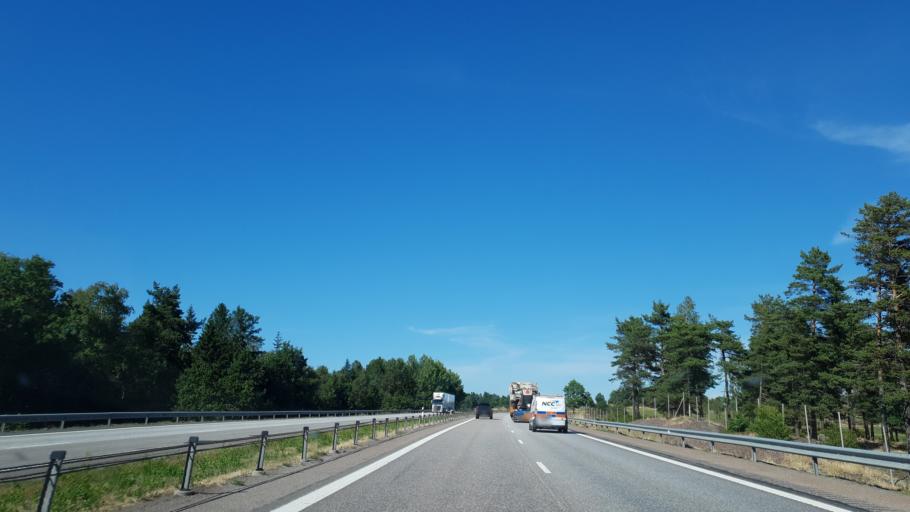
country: SE
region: OEstergoetland
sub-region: Odeshogs Kommun
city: OEdeshoeg
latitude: 58.1926
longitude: 14.6093
